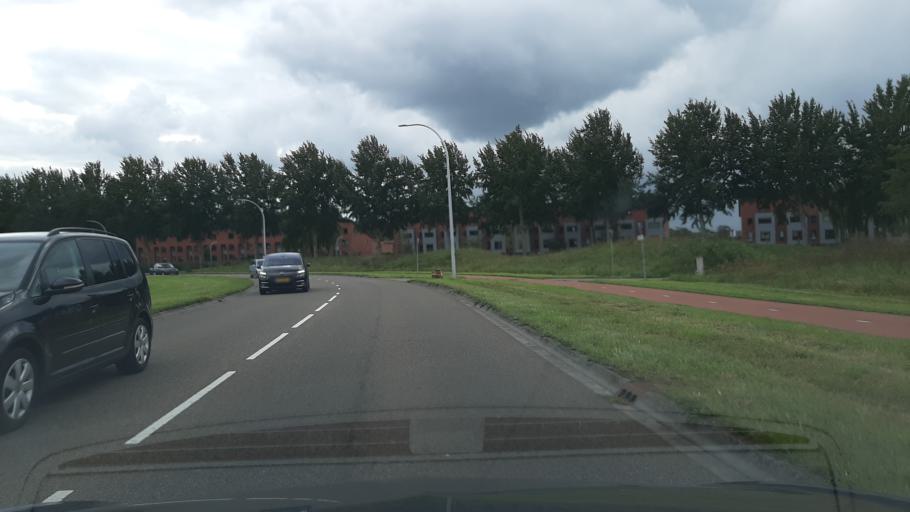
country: NL
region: Overijssel
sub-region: Gemeente Zwolle
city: Zwolle
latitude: 52.5371
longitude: 6.0657
